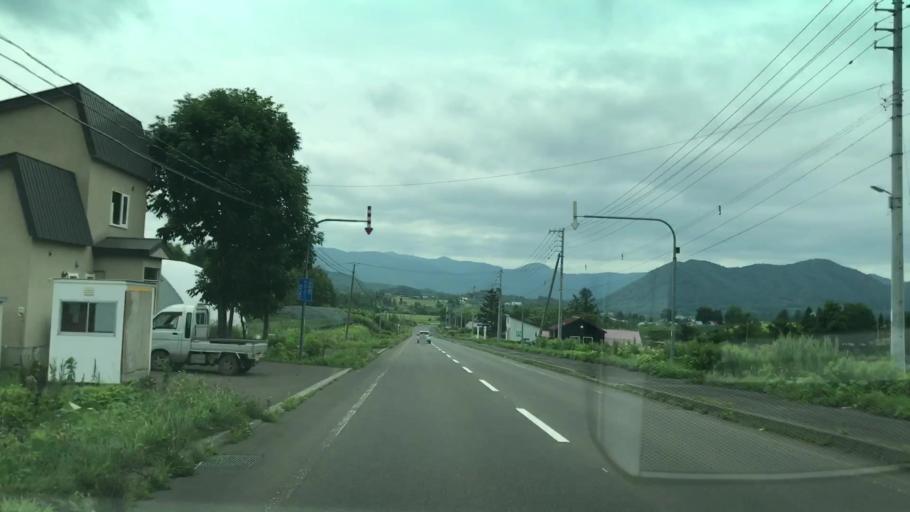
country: JP
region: Hokkaido
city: Yoichi
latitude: 43.1039
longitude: 140.8235
